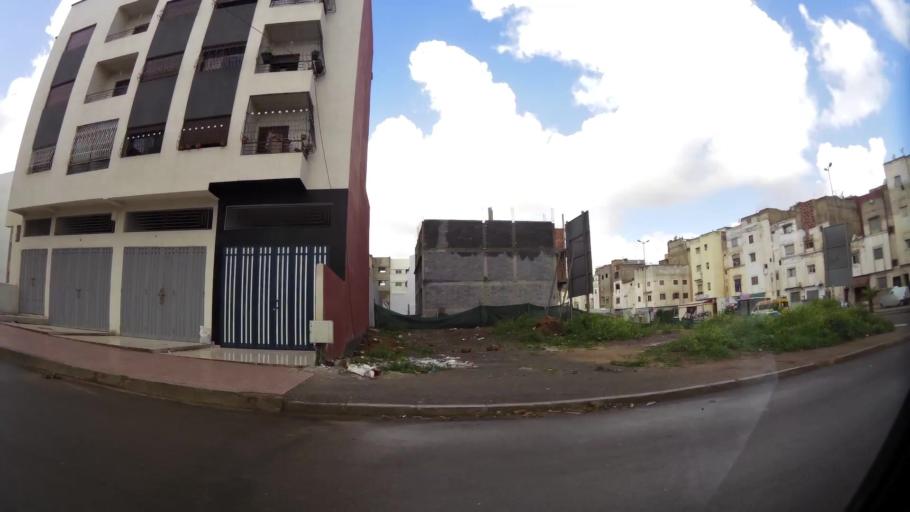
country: MA
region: Grand Casablanca
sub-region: Mediouna
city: Tit Mellil
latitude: 33.5482
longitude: -7.4836
